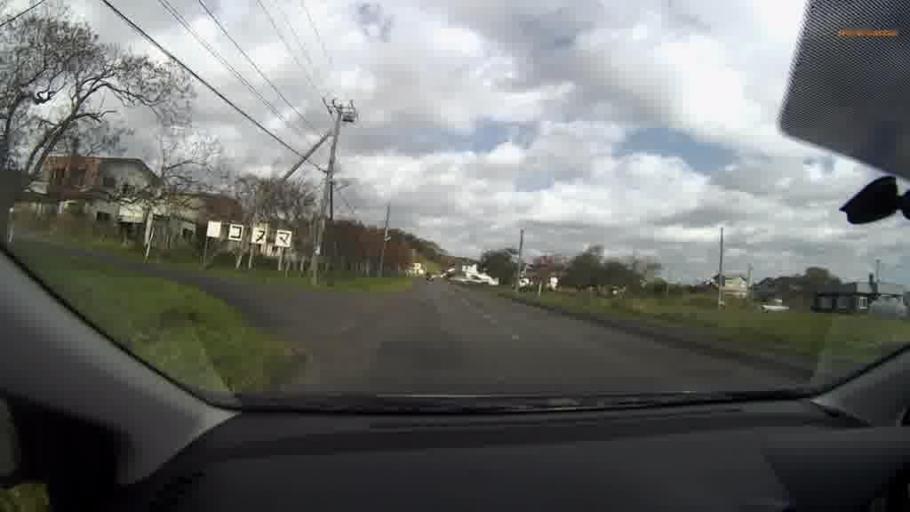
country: JP
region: Hokkaido
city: Kushiro
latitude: 42.9737
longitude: 144.1244
